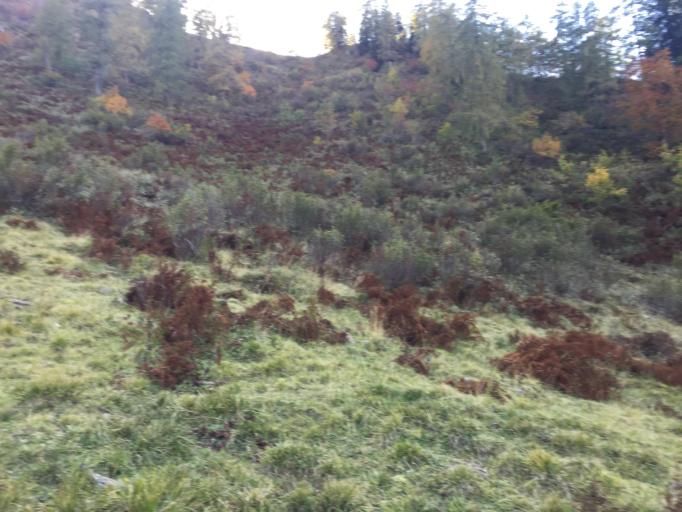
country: IT
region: Friuli Venezia Giulia
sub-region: Provincia di Udine
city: Sauris di Sotto
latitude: 46.4993
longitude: 12.7420
